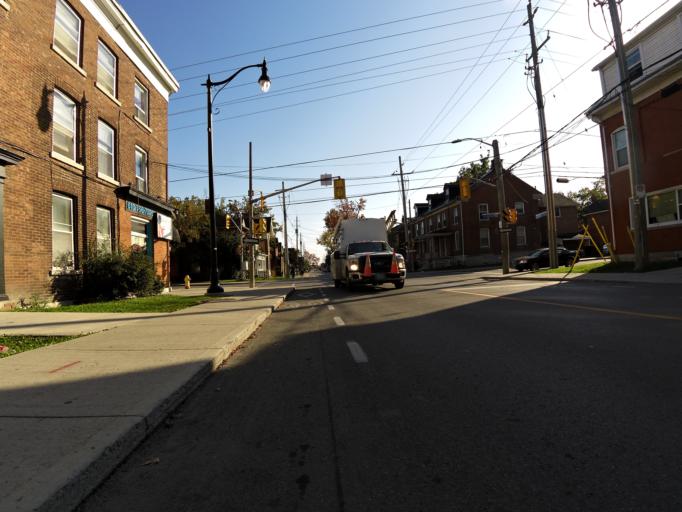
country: CA
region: Ontario
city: Kingston
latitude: 44.2319
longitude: -76.4956
